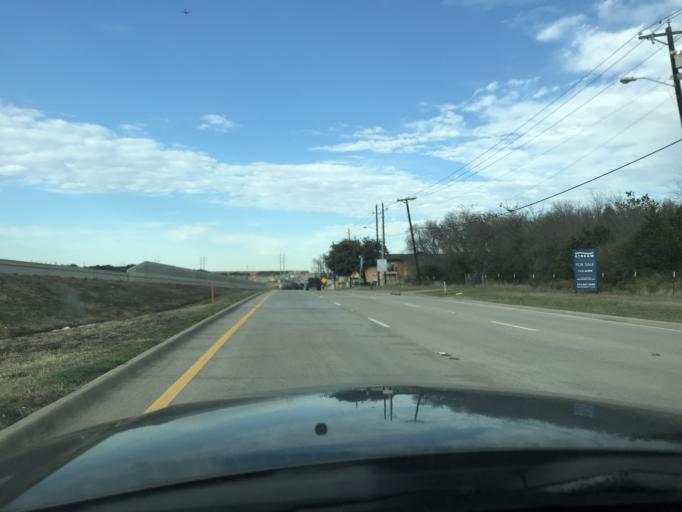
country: US
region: Texas
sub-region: Dallas County
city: Grand Prairie
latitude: 32.7119
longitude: -97.0242
